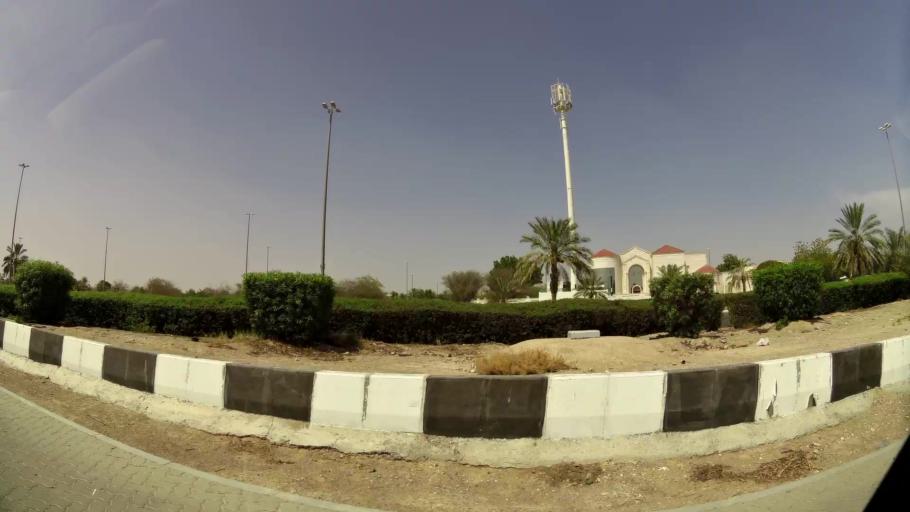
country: AE
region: Abu Dhabi
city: Al Ain
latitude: 24.2325
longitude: 55.7072
